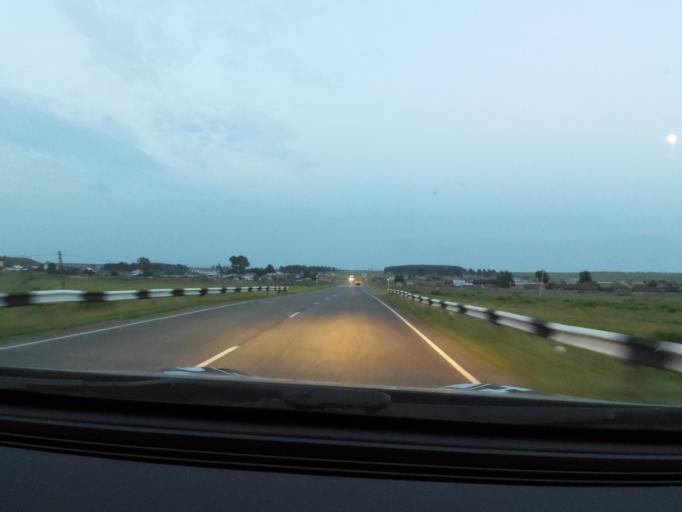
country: RU
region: Sverdlovsk
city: Sarana
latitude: 56.1308
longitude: 58.0104
